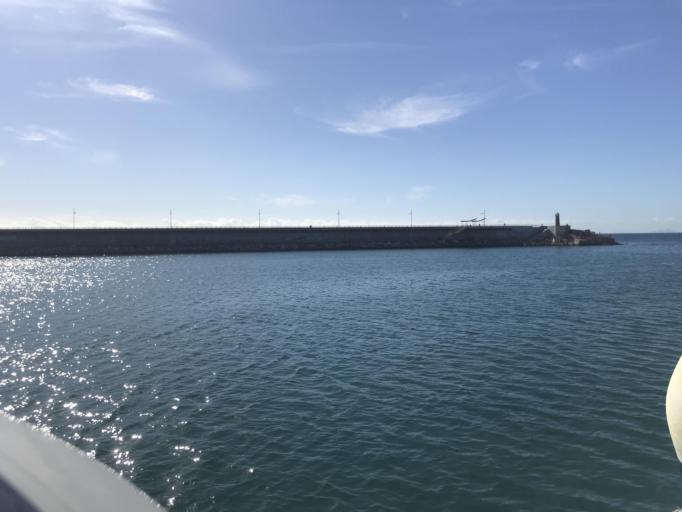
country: ES
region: Valencia
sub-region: Provincia de Alicante
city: Torrevieja
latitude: 37.9670
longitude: -0.6872
